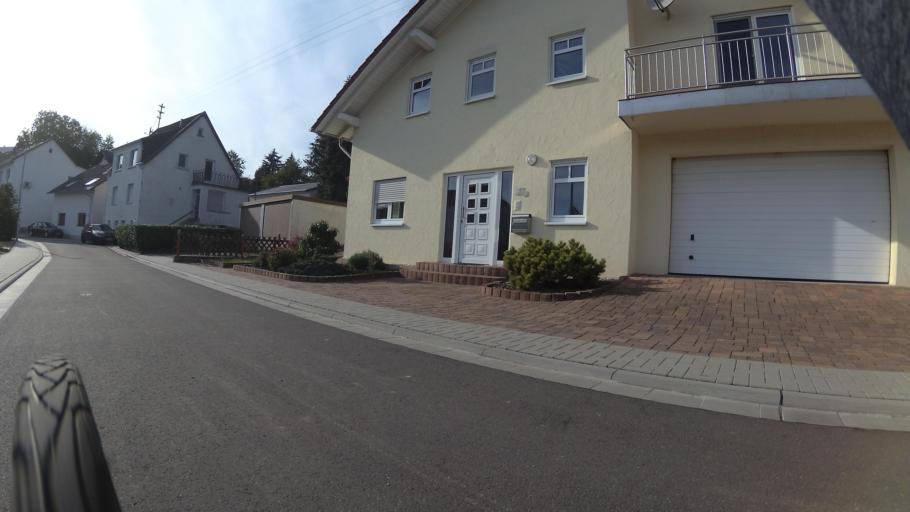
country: DE
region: Rheinland-Pfalz
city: Wahnwegen
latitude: 49.4558
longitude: 7.3836
